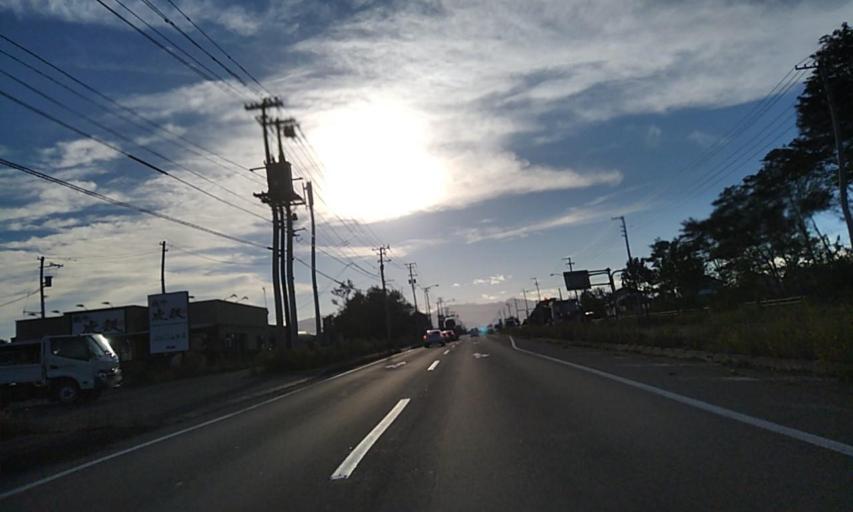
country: JP
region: Hokkaido
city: Obihiro
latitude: 42.9219
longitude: 143.0639
